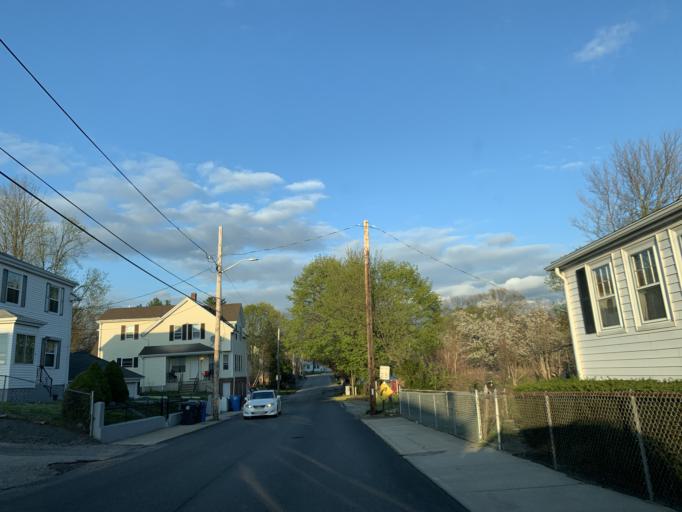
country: US
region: Rhode Island
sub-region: Providence County
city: Valley Falls
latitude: 41.8997
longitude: -71.3822
